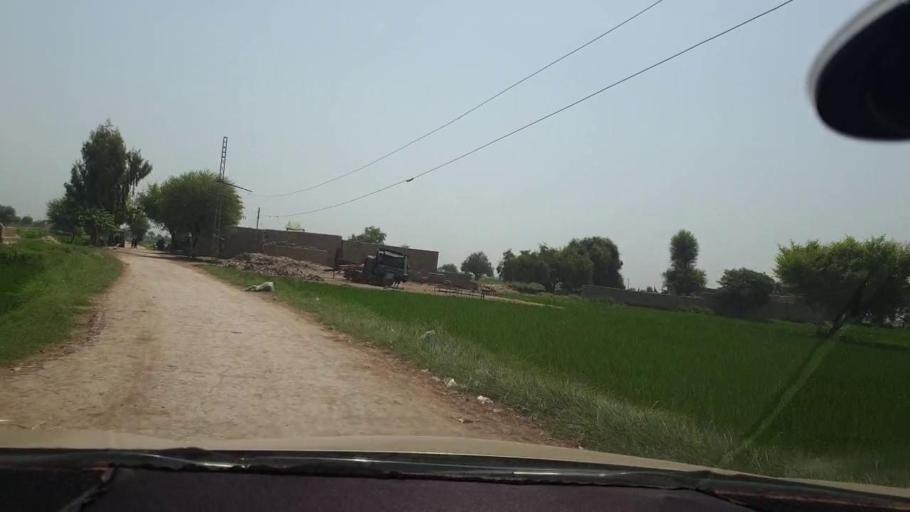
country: PK
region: Sindh
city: Kambar
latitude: 27.6335
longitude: 67.9322
